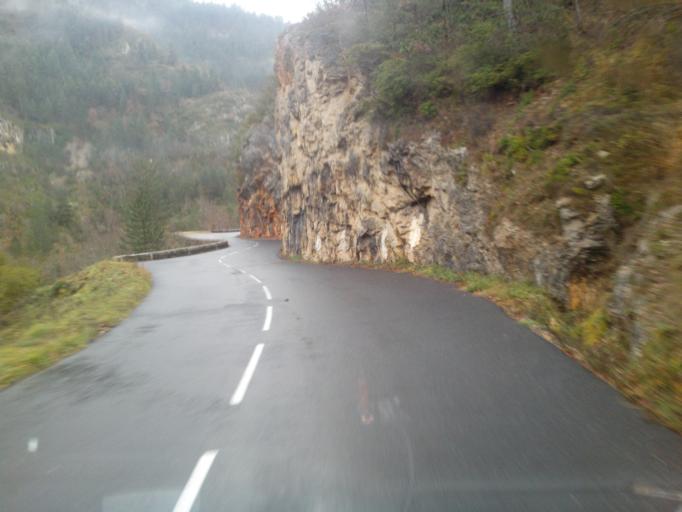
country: FR
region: Languedoc-Roussillon
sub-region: Departement de la Lozere
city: Chanac
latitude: 44.3437
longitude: 3.3886
